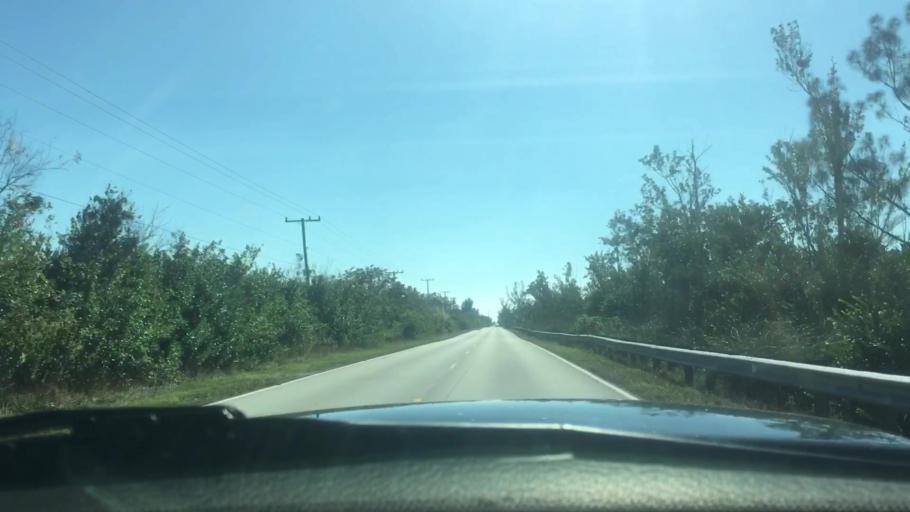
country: US
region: Florida
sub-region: Miami-Dade County
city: Florida City
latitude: 25.3713
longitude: -80.4327
